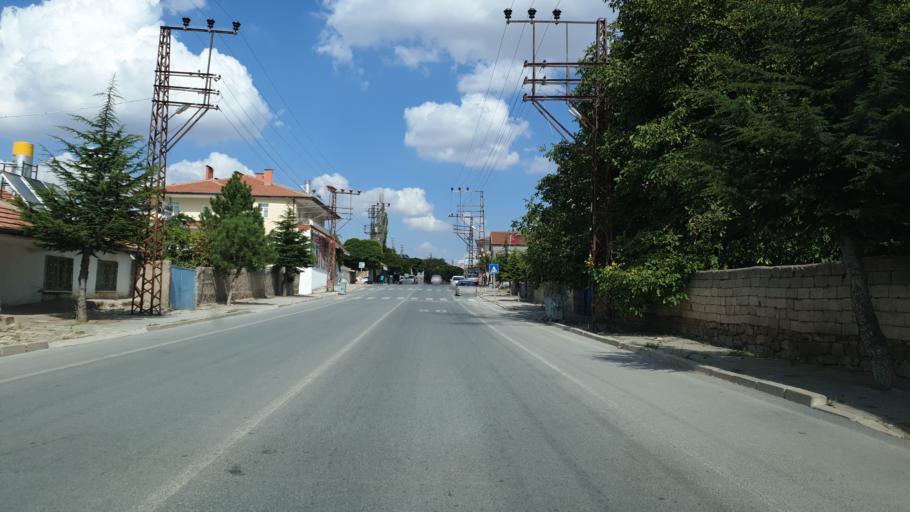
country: TR
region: Kayseri
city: Felahiye
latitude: 39.0894
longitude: 35.5657
